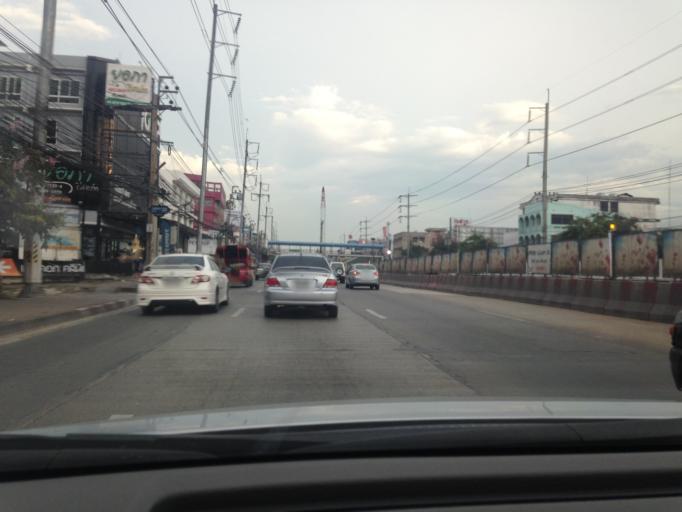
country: TH
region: Bangkok
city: Bang Khen
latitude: 13.8589
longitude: 100.6254
